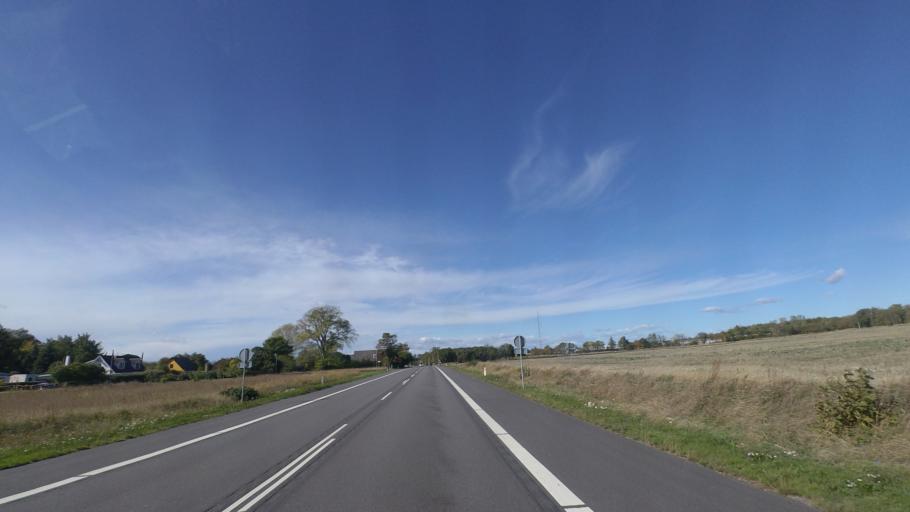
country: DK
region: Capital Region
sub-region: Bornholm Kommune
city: Ronne
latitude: 55.0884
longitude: 14.7412
